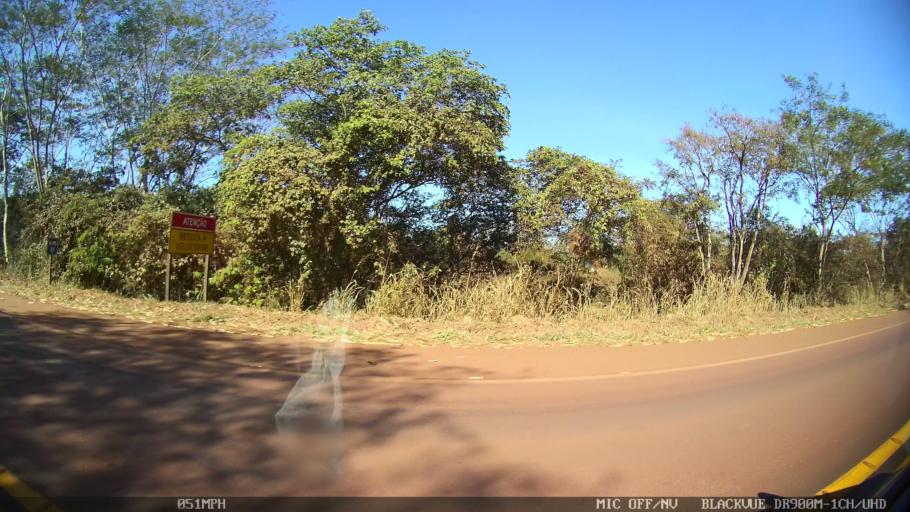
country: BR
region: Sao Paulo
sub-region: Barretos
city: Barretos
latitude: -20.4552
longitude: -48.4596
